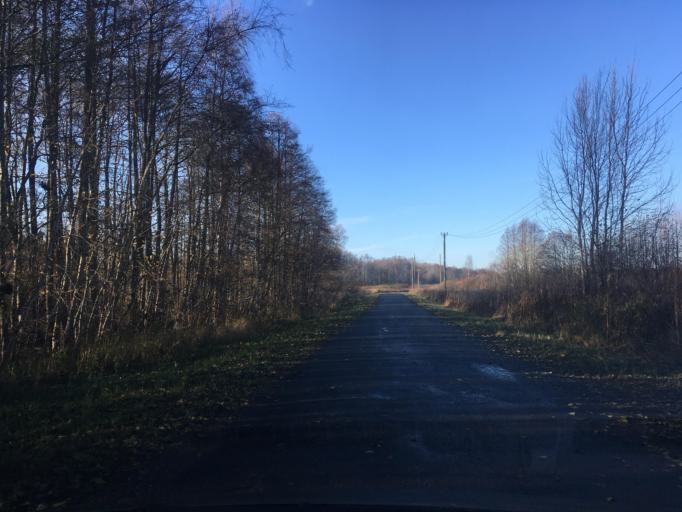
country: EE
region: Harju
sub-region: Maardu linn
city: Maardu
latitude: 59.4762
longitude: 25.1179
